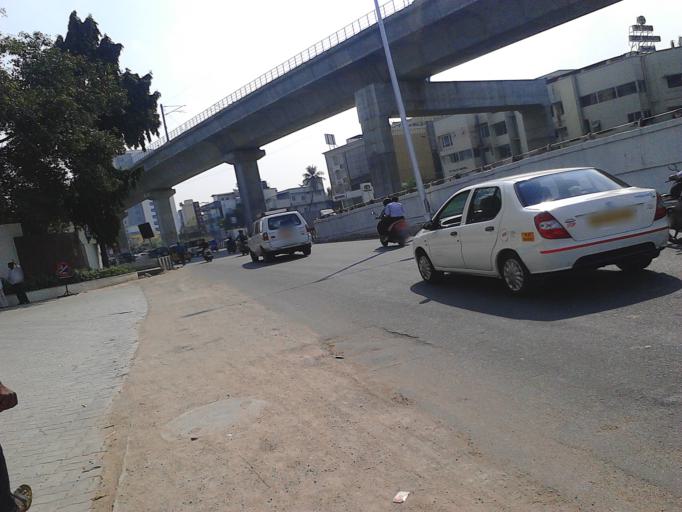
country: IN
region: Tamil Nadu
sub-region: Kancheepuram
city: Alandur
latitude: 13.0078
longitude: 80.2055
